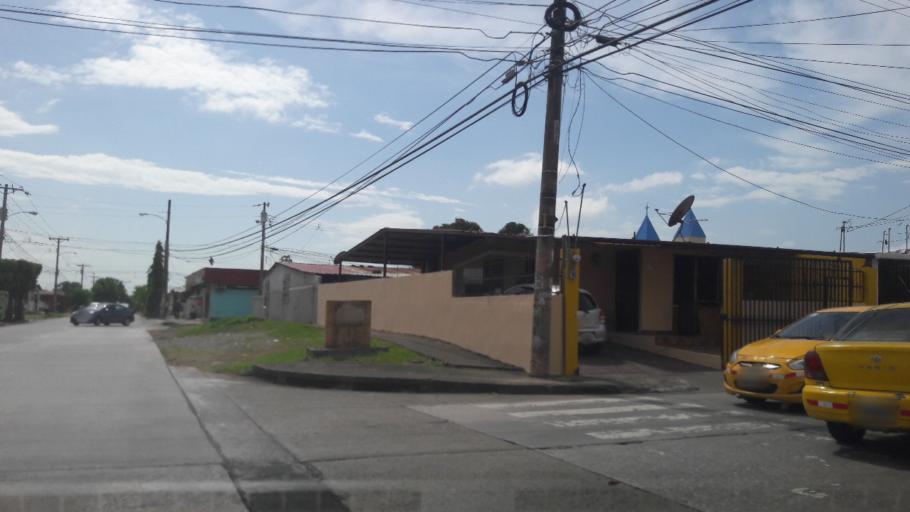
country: PA
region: Panama
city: Tocumen
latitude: 9.0551
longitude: -79.4170
